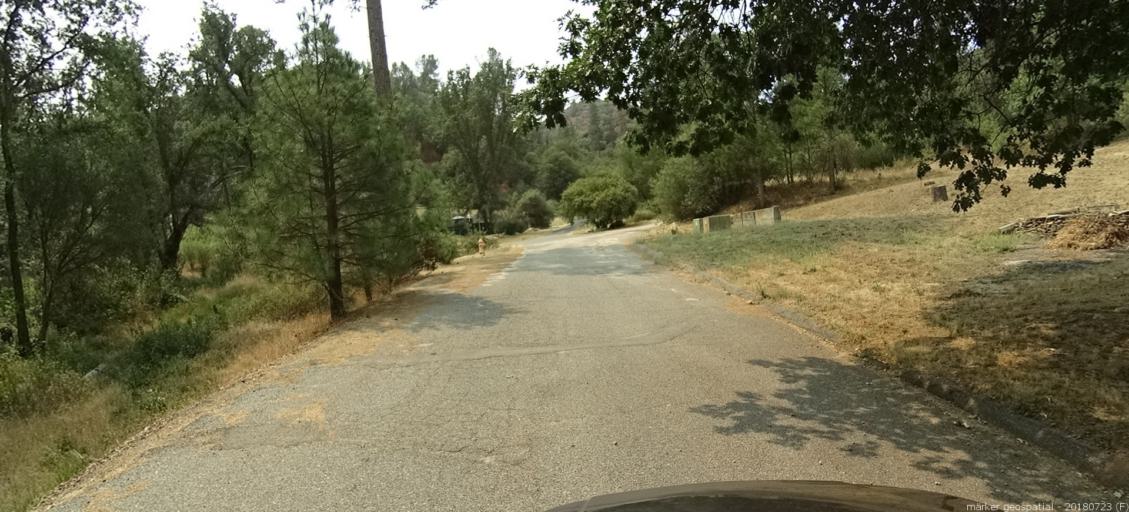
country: US
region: California
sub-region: Madera County
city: Ahwahnee
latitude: 37.3323
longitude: -119.7087
